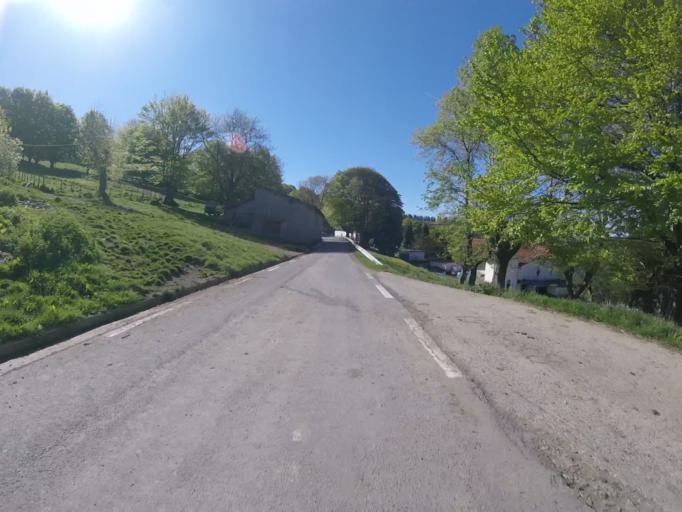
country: ES
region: Basque Country
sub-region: Provincia de Guipuzcoa
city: Errezil
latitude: 43.1990
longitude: -2.2014
